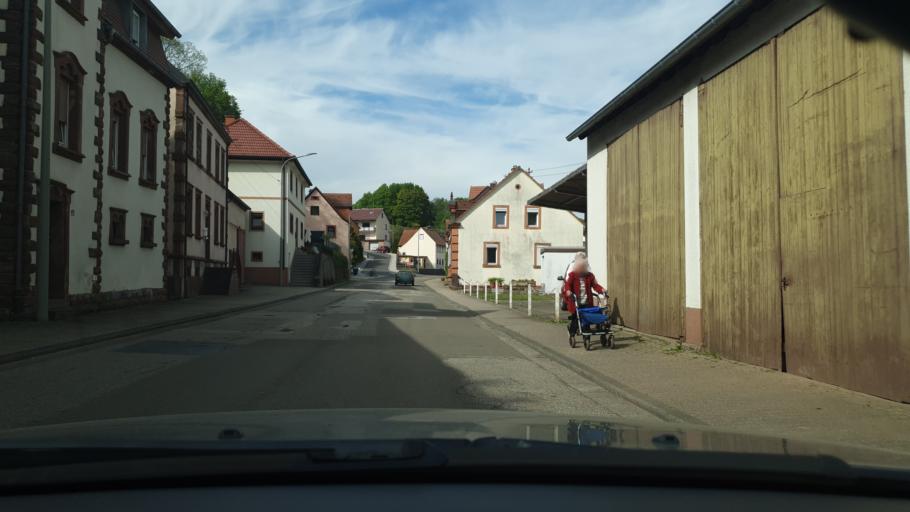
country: DE
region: Rheinland-Pfalz
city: Wallhalben
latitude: 49.3182
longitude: 7.5217
